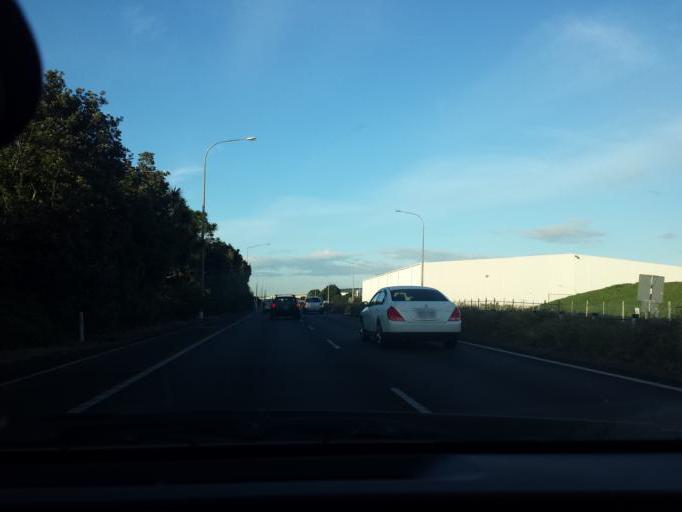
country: NZ
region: Auckland
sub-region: Auckland
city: Mangere
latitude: -36.9772
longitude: 174.7872
